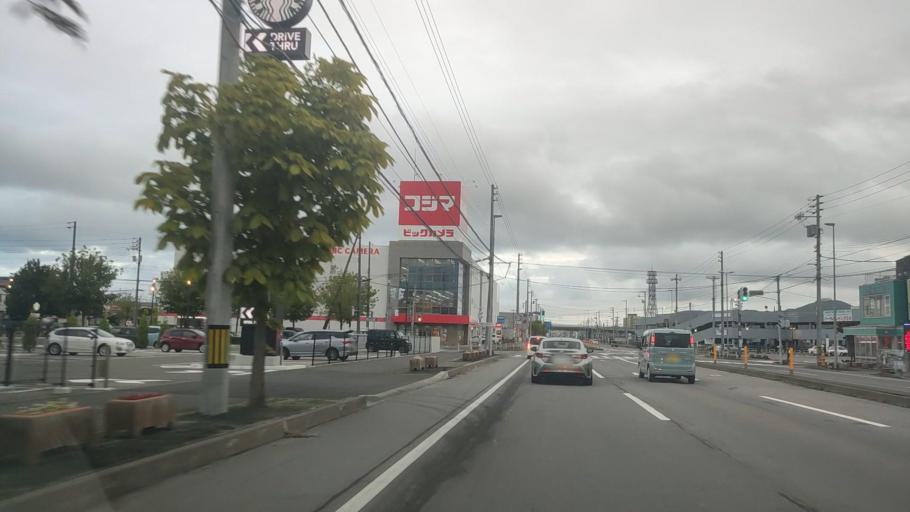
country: JP
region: Hokkaido
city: Hakodate
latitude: 41.8043
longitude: 140.7349
